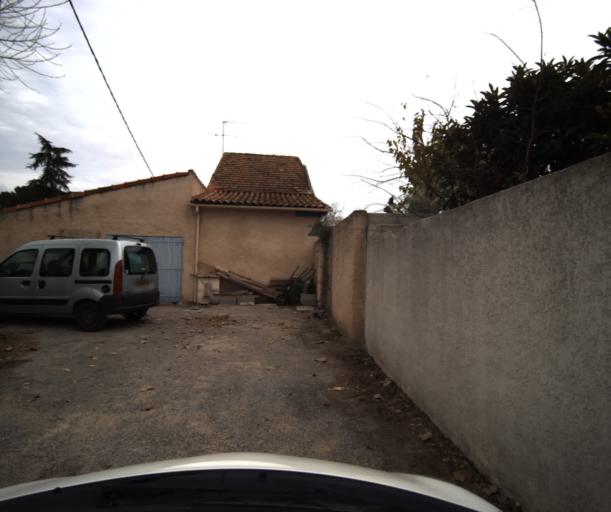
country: FR
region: Provence-Alpes-Cote d'Azur
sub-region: Departement du Vaucluse
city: Pertuis
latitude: 43.6935
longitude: 5.5071
